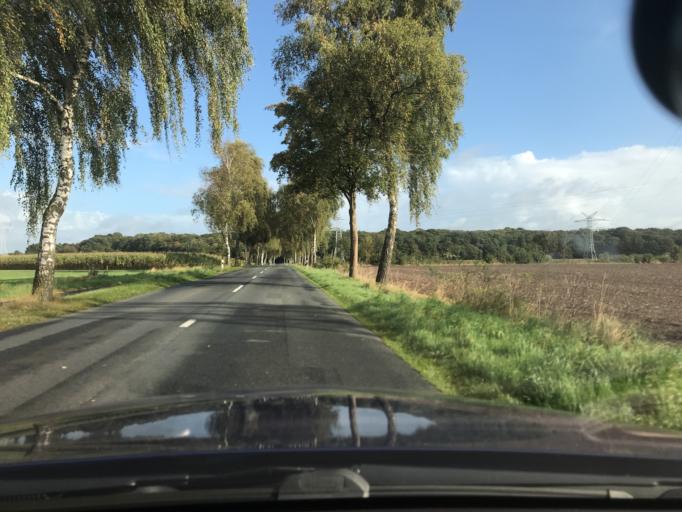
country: DE
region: Lower Saxony
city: Ahlerstedt
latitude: 53.4141
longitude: 9.4593
